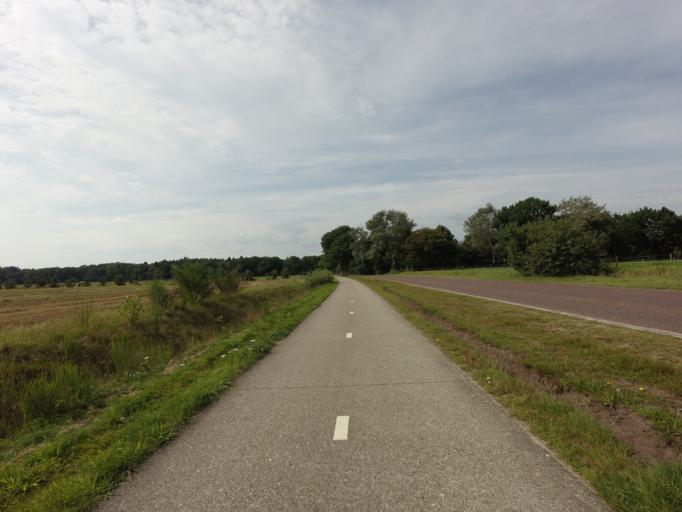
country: NL
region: Drenthe
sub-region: Gemeente Westerveld
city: Dwingeloo
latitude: 52.9111
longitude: 6.2801
